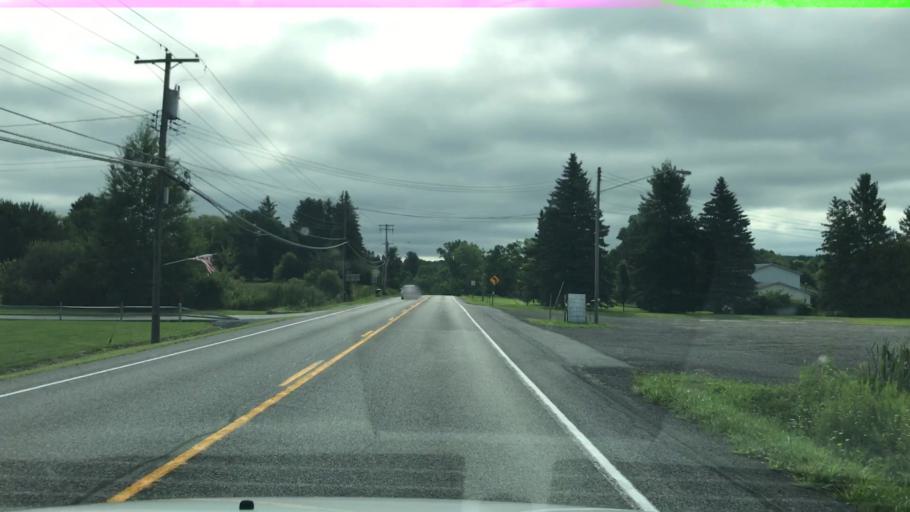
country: US
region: New York
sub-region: Wyoming County
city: Attica
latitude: 42.8364
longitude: -78.3928
